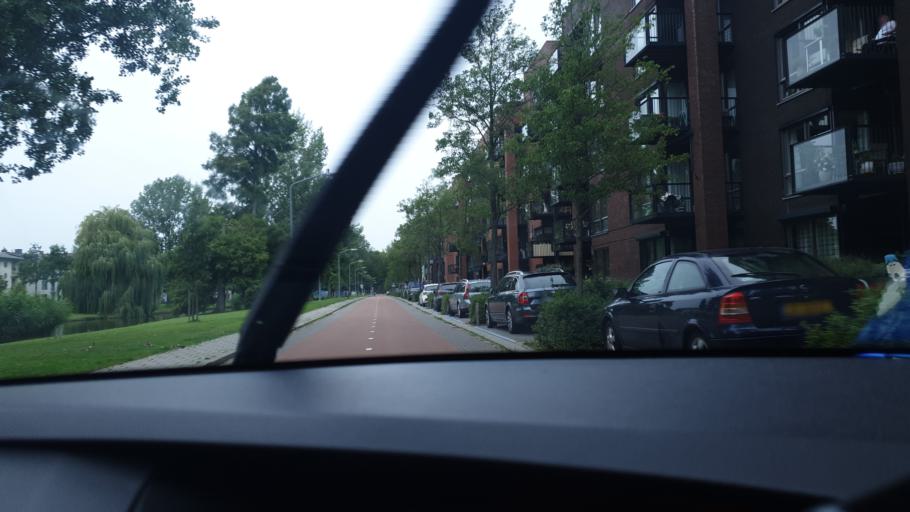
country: NL
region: South Holland
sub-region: Gemeente Dordrecht
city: Dordrecht
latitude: 51.8019
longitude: 4.6714
